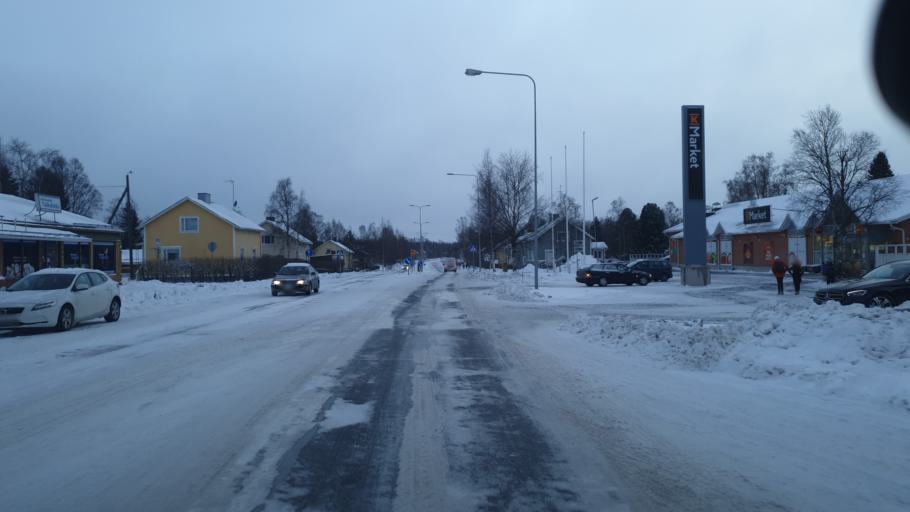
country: FI
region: Lapland
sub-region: Kemi-Tornio
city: Kemi
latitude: 65.7297
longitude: 24.6009
